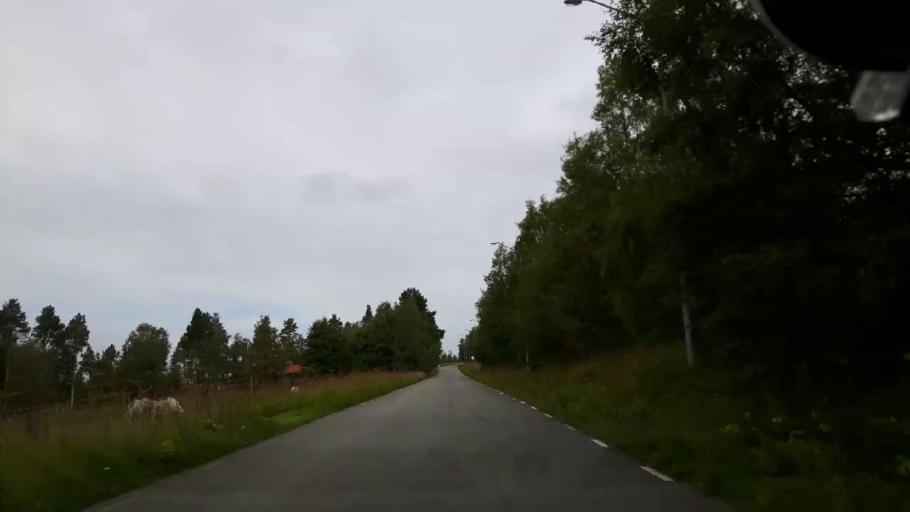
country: SE
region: Jaemtland
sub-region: OEstersunds Kommun
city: Ostersund
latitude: 63.1743
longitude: 14.5166
